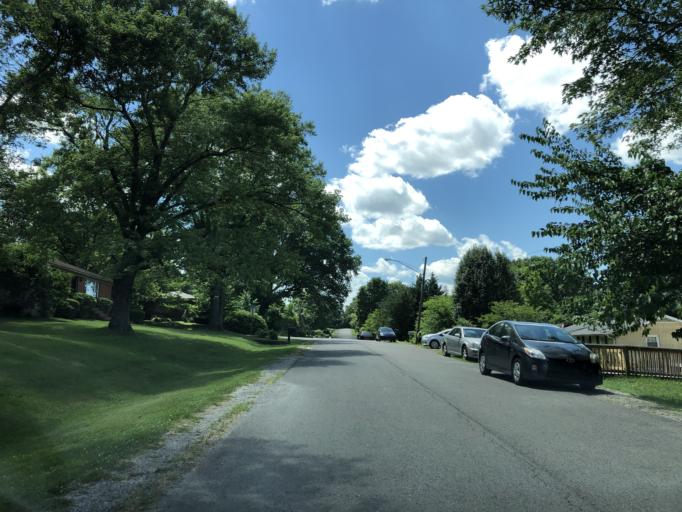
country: US
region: Tennessee
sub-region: Davidson County
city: Nashville
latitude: 36.1744
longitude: -86.7225
